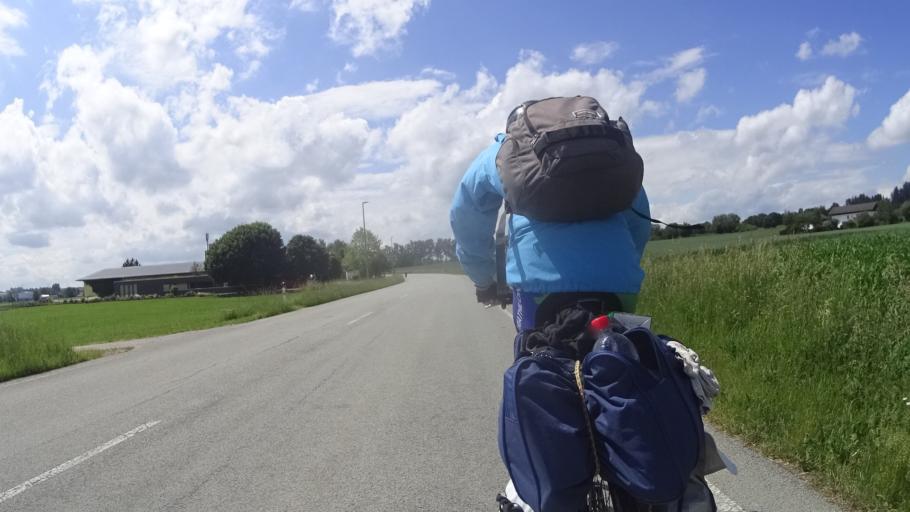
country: DE
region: Bavaria
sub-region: Lower Bavaria
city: Unterdietfurt
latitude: 48.3945
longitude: 12.6630
